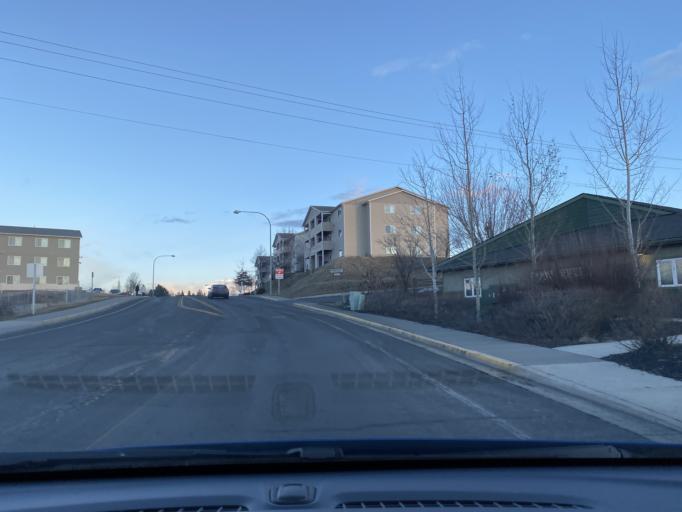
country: US
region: Idaho
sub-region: Latah County
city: Moscow
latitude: 46.7358
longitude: -117.0232
